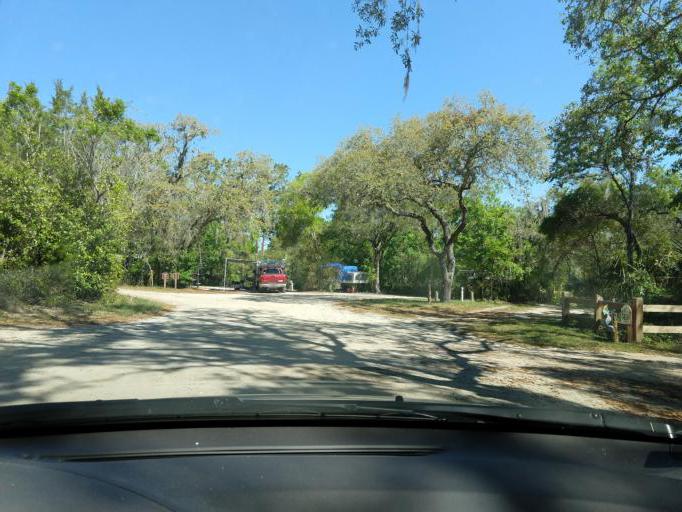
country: US
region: Florida
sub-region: Lake County
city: Fruitland Park
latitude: 28.8600
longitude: -81.9019
